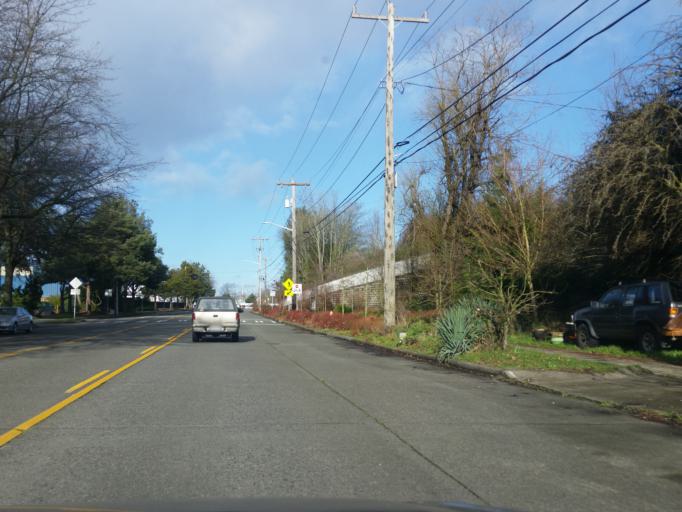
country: US
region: Washington
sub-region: King County
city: Seattle
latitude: 47.6755
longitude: -122.4064
